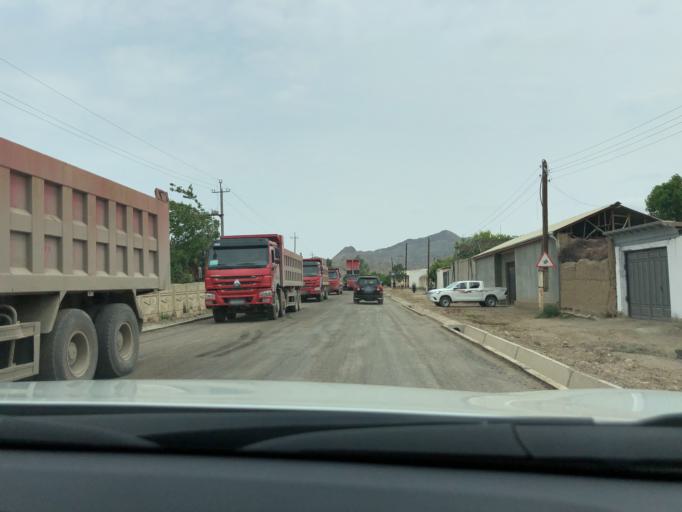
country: TJ
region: Viloyati Sughd
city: Isfara
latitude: 40.1578
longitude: 70.6305
